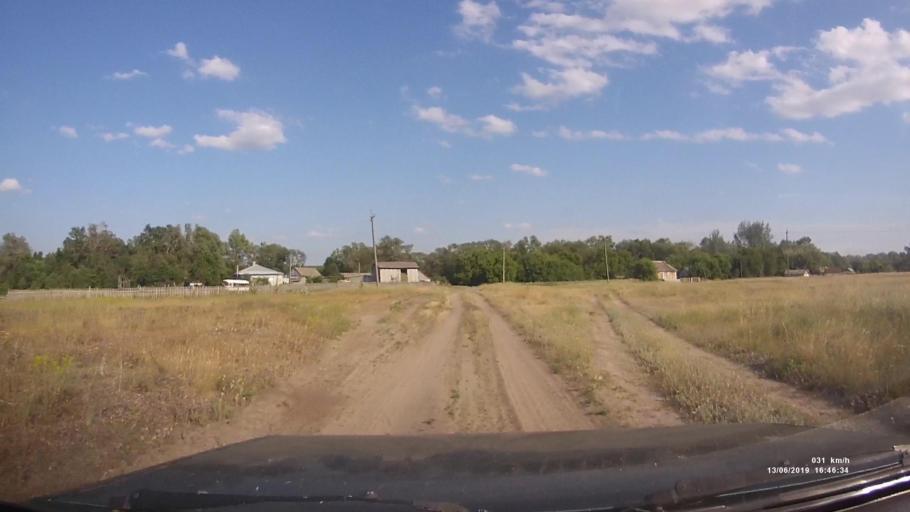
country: RU
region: Rostov
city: Kazanskaya
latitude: 49.9453
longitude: 41.4280
